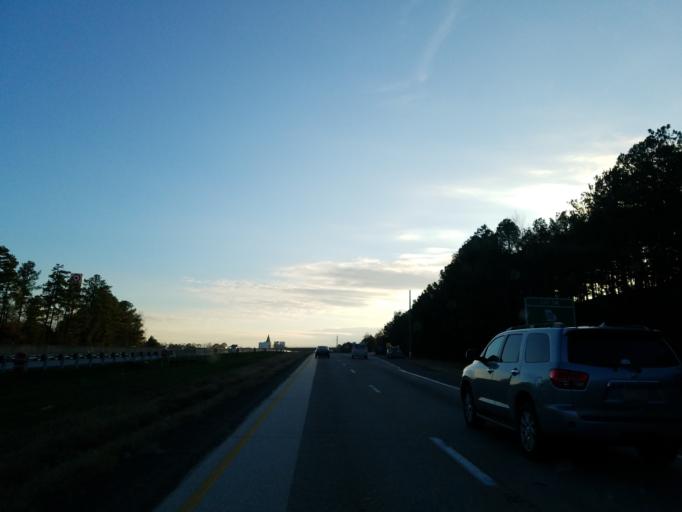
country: US
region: Georgia
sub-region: Forsyth County
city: Cumming
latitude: 34.1889
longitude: -84.1356
